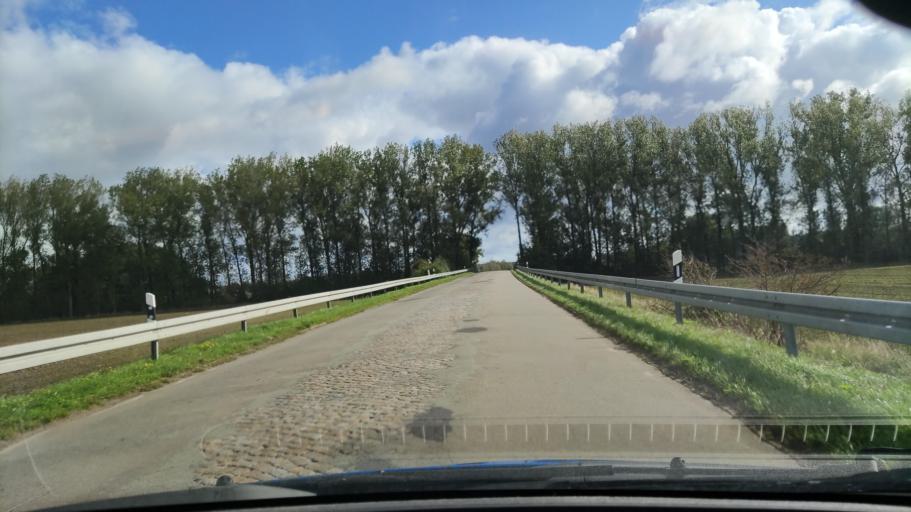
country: DE
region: Saxony-Anhalt
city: Salzwedel
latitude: 52.8536
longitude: 11.1977
